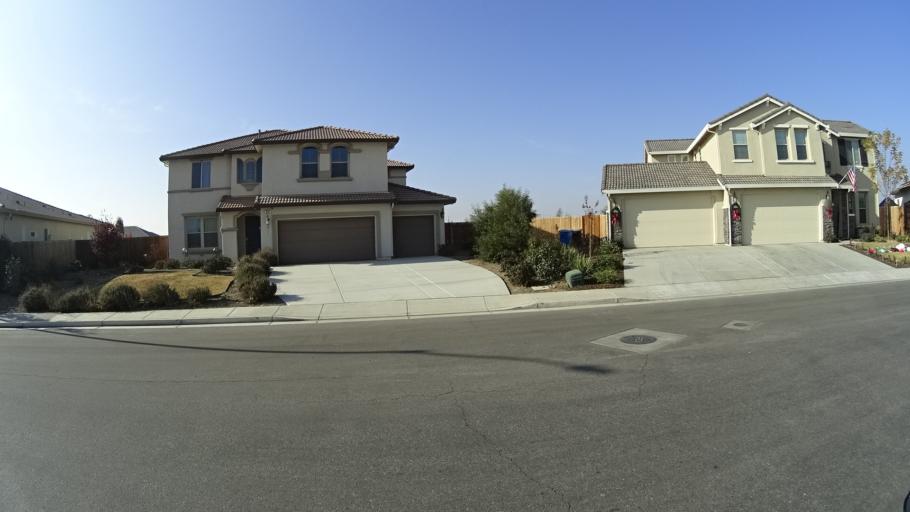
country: US
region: California
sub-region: Kern County
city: Rosedale
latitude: 35.3496
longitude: -119.1724
